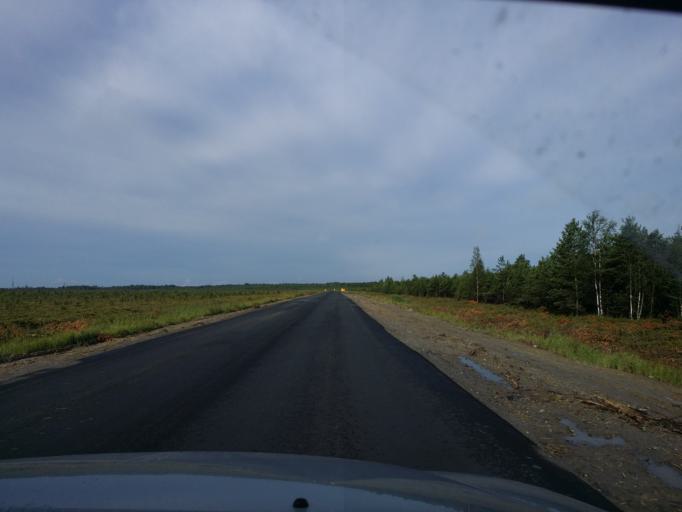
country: RU
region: Tjumen
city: Uvat
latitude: 59.3664
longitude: 69.0004
